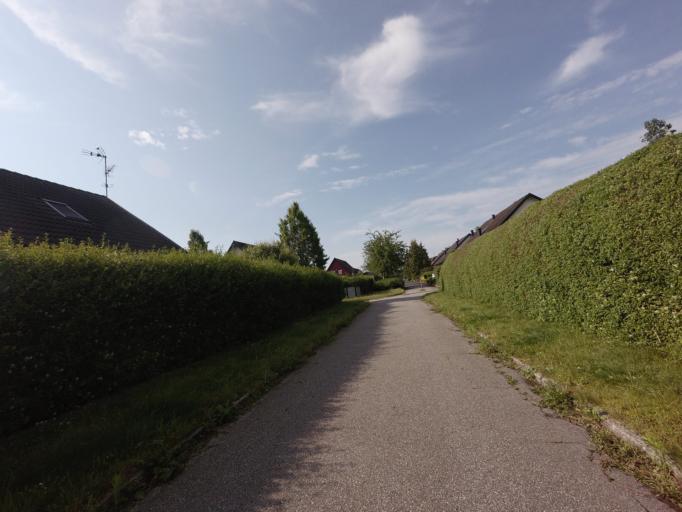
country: SE
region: Skane
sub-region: Trelleborgs Kommun
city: Trelleborg
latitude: 55.3644
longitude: 13.2234
